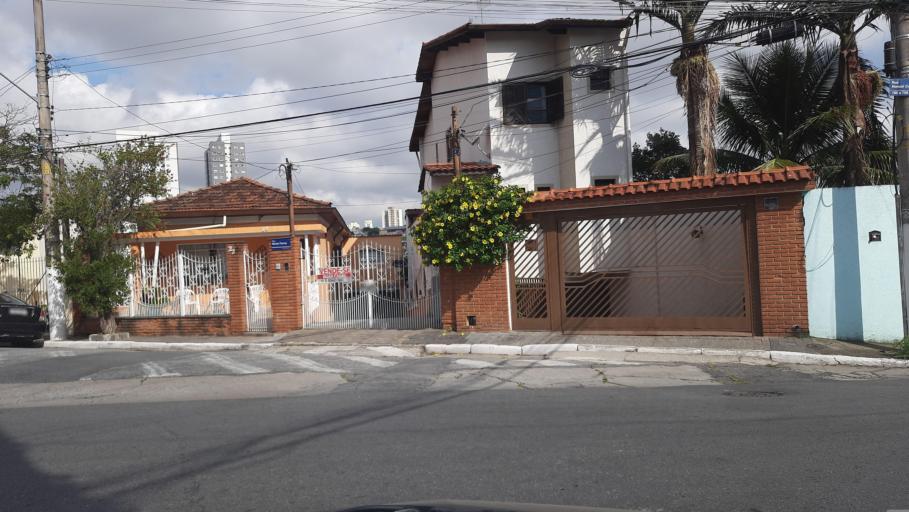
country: BR
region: Sao Paulo
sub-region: Sao Paulo
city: Sao Paulo
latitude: -23.4951
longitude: -46.6888
